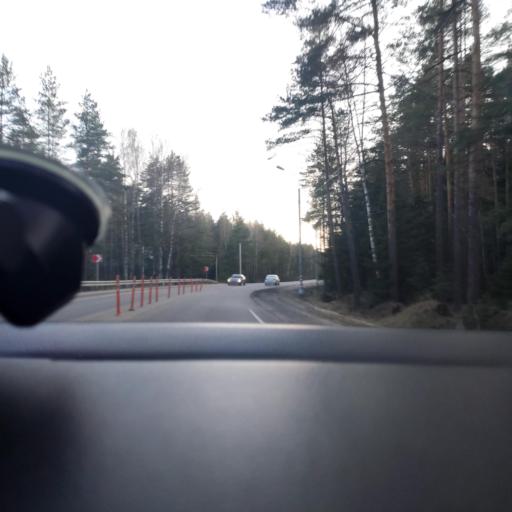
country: RU
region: Moskovskaya
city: Krasnyy Tkach
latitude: 55.4117
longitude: 39.1696
